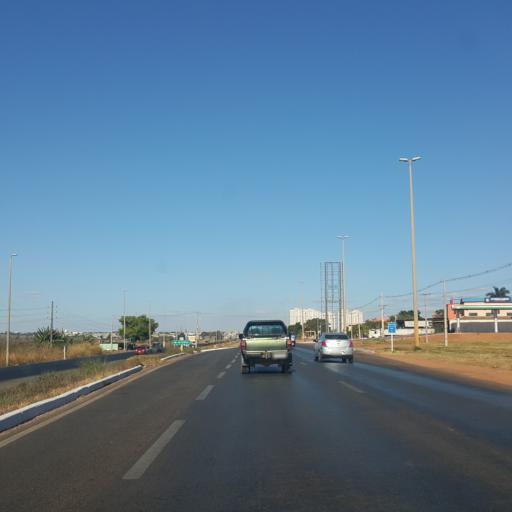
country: BR
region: Federal District
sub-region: Brasilia
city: Brasilia
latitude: -15.7910
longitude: -48.1063
